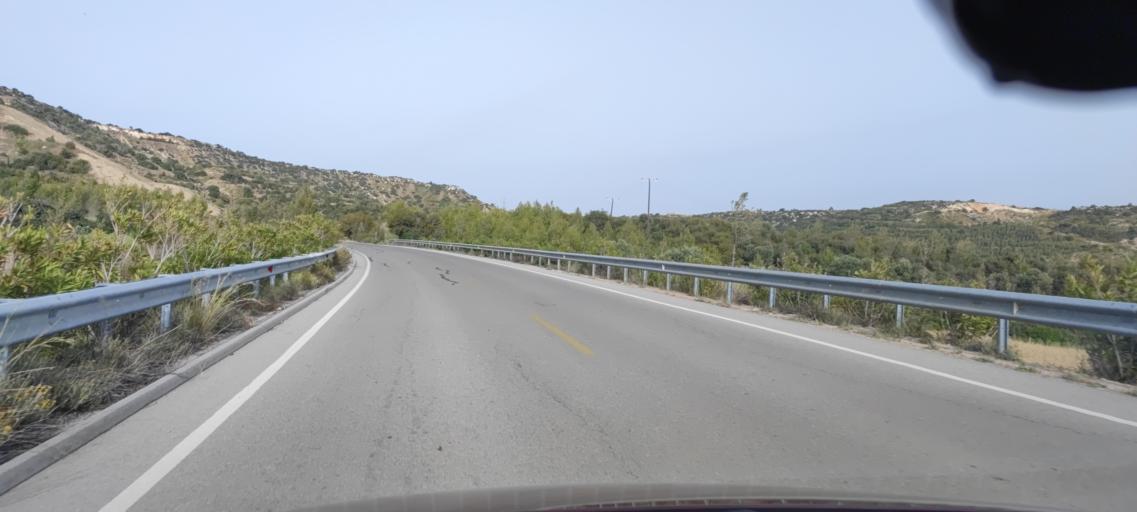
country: CY
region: Ammochostos
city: Leonarisso
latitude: 35.4774
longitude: 34.1241
